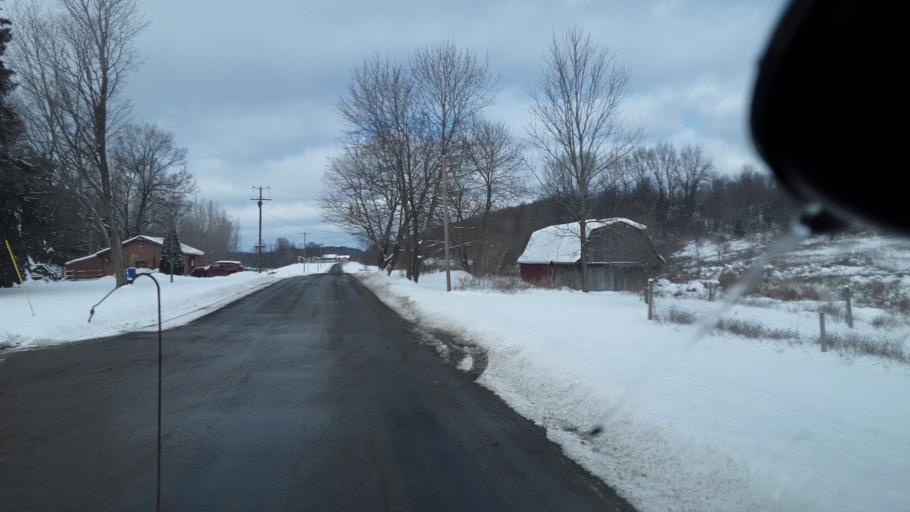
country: US
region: New York
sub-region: Wayne County
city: Lyons
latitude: 43.1047
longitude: -77.0448
